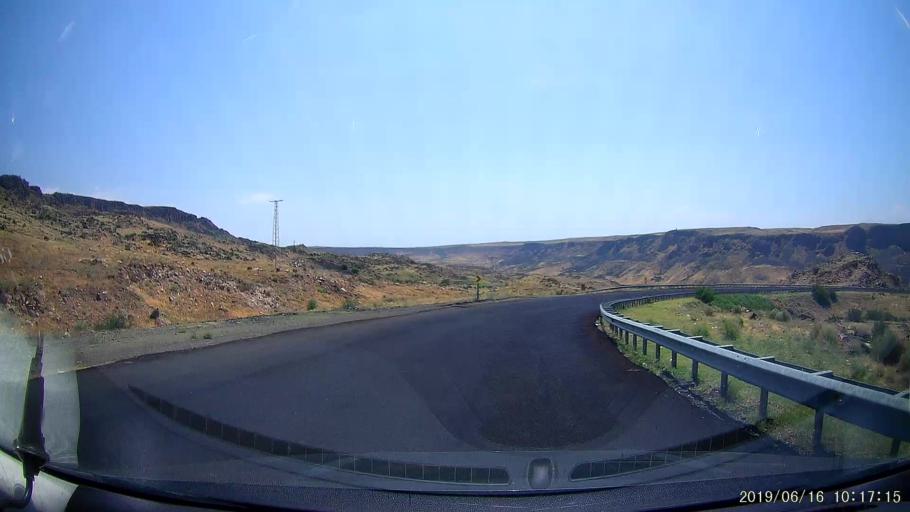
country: TR
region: Igdir
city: Tuzluca
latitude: 40.1694
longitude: 43.6817
